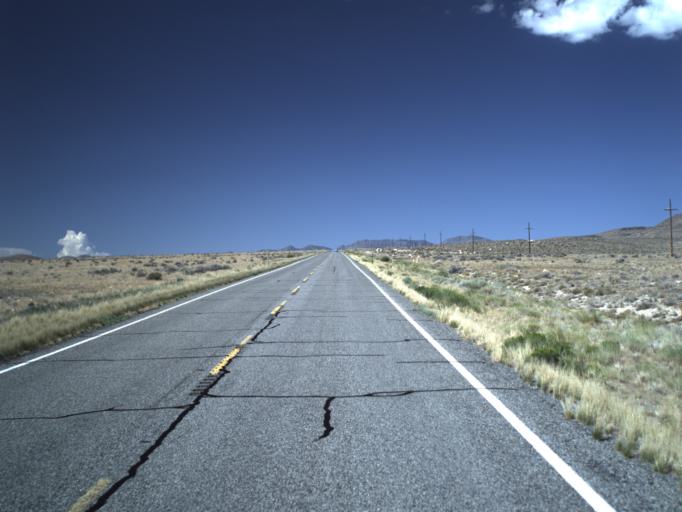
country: US
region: Utah
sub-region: Beaver County
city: Milford
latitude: 39.0542
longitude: -113.2622
